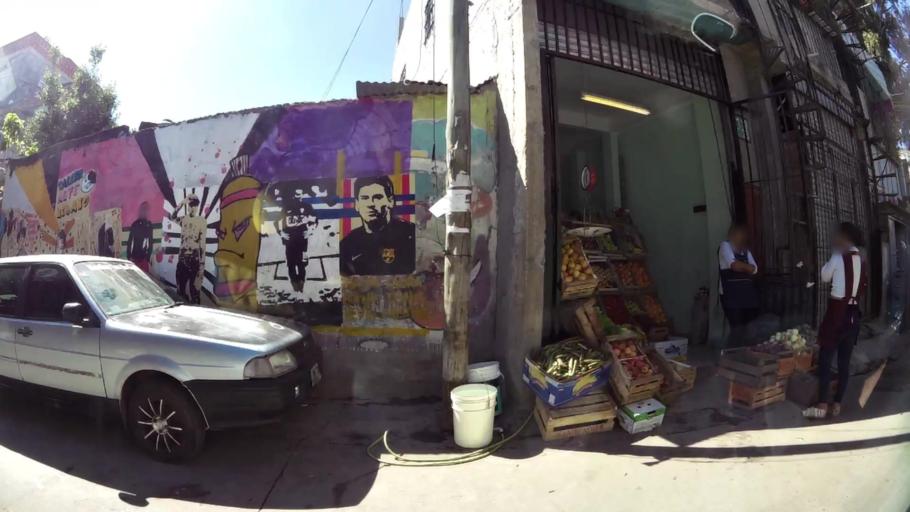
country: AR
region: Buenos Aires F.D.
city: Retiro
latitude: -34.5827
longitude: -58.3796
